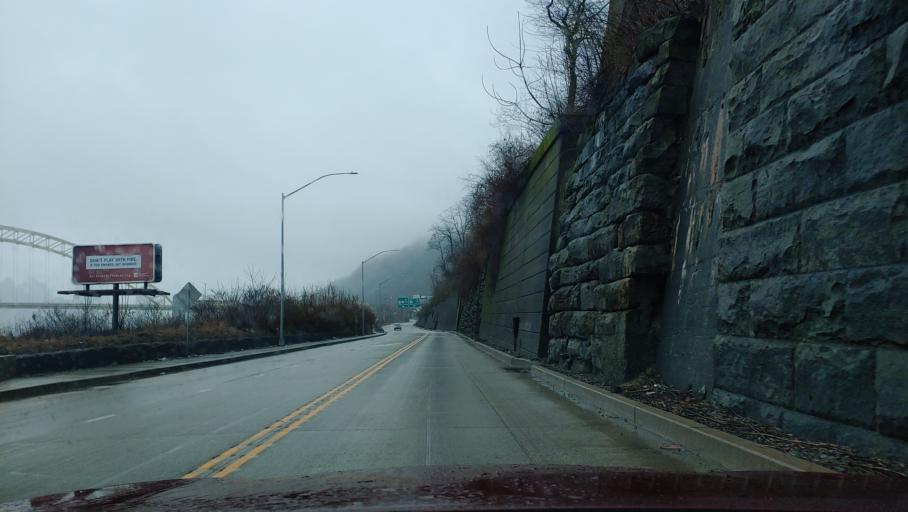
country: US
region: Pennsylvania
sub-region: Allegheny County
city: Ingram
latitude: 40.4475
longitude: -80.0327
